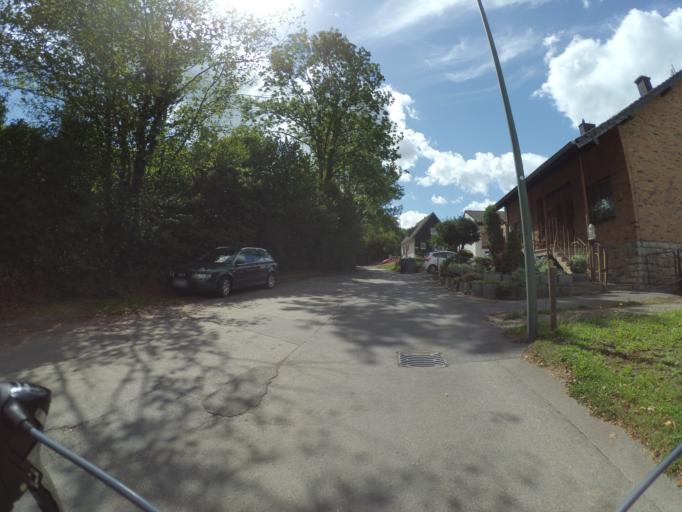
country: DE
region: North Rhine-Westphalia
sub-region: Regierungsbezirk Koln
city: Eschweiler
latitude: 50.7688
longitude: 6.3021
